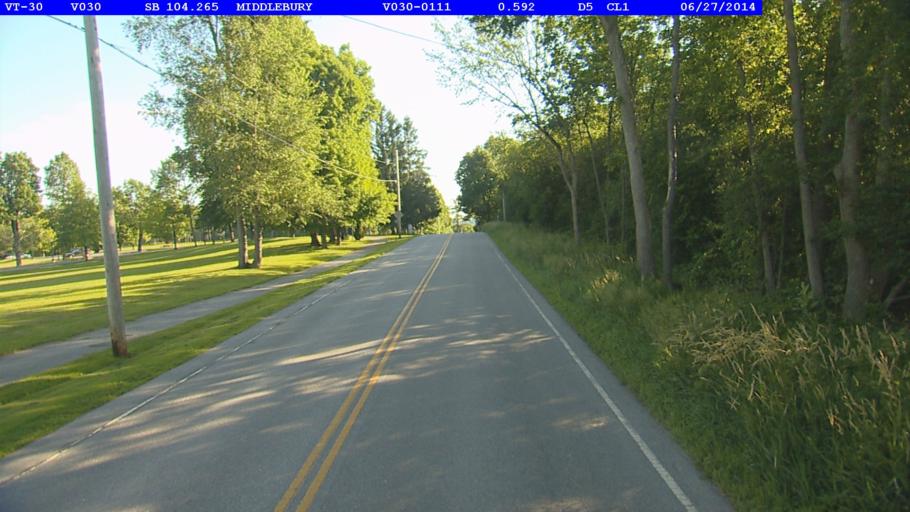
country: US
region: Vermont
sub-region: Addison County
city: Middlebury (village)
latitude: 44.0019
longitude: -73.1817
